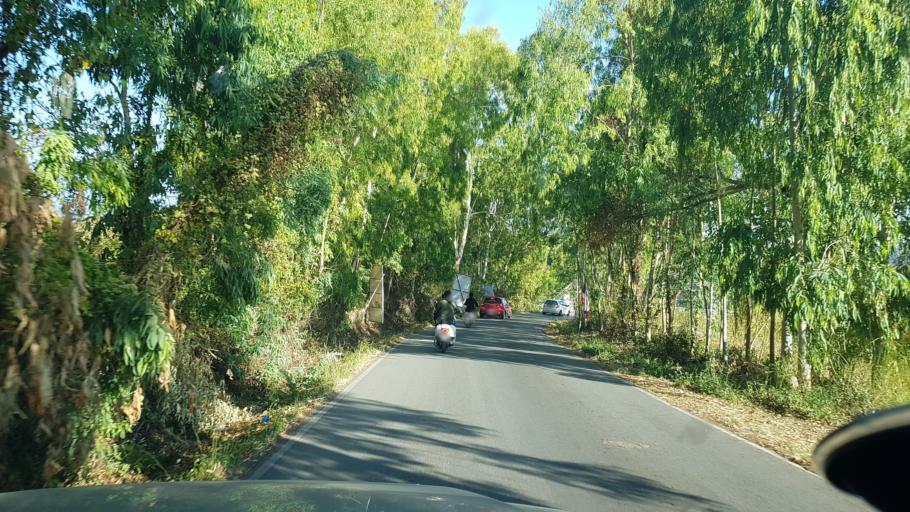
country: TH
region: Phetchabun
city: Khao Kho
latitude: 16.7726
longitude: 101.0550
